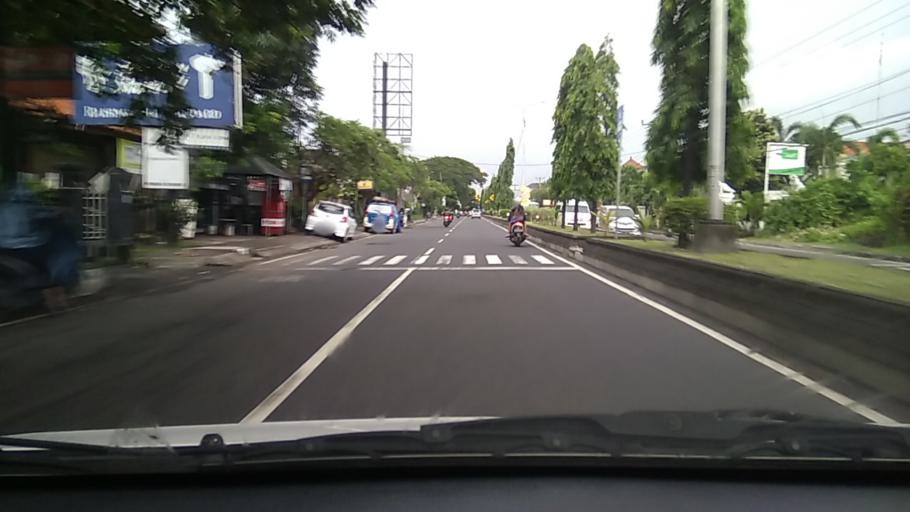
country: ID
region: Bali
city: Banjar Medura
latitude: -8.6913
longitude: 115.2587
